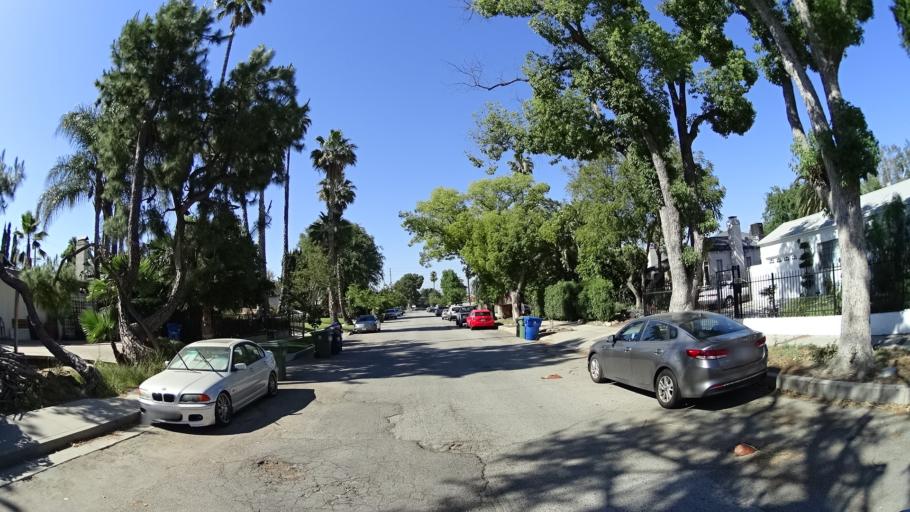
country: US
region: California
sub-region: Los Angeles County
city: North Hollywood
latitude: 34.1744
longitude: -118.3639
